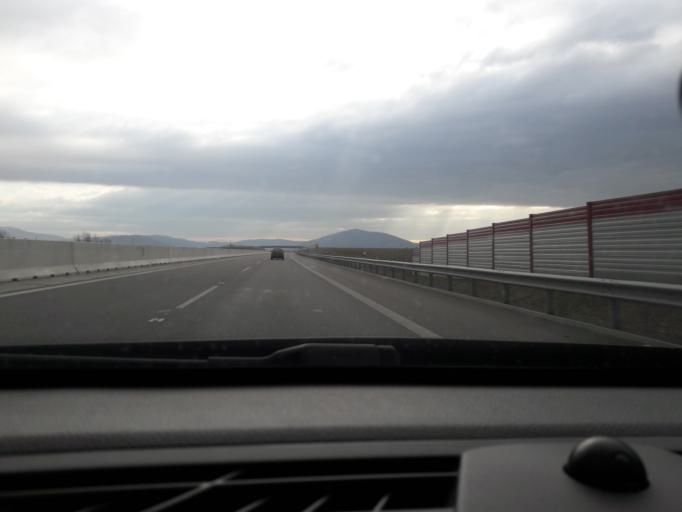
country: SK
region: Banskobystricky
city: Hrochot,Slovakia
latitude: 48.5719
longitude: 19.2671
